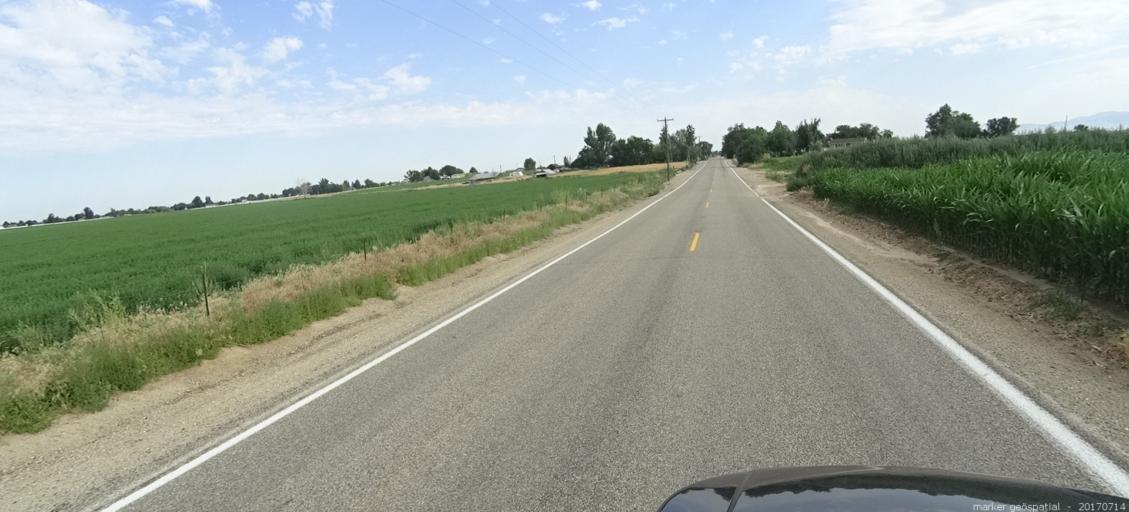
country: US
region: Idaho
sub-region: Ada County
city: Kuna
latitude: 43.4689
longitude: -116.3545
